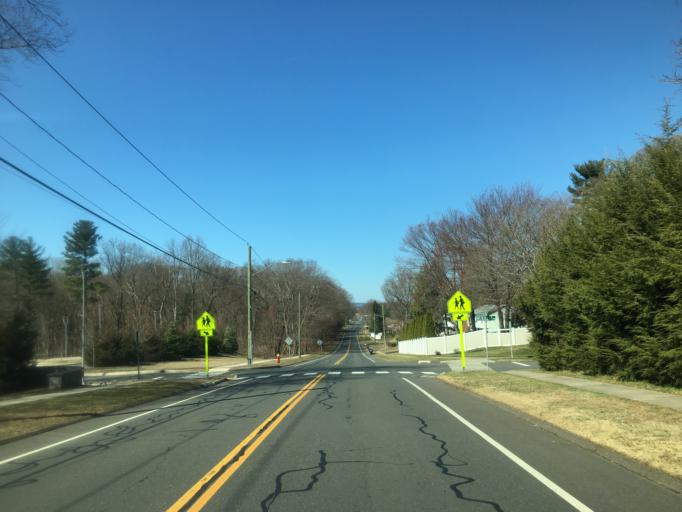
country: US
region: Connecticut
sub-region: Hartford County
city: East Hartford
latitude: 41.8065
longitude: -72.5953
